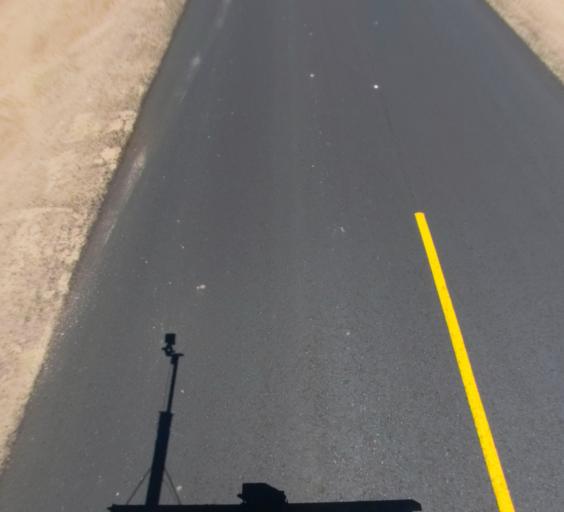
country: US
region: California
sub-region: Madera County
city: Bonadelle Ranchos-Madera Ranchos
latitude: 36.8962
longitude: -119.8575
